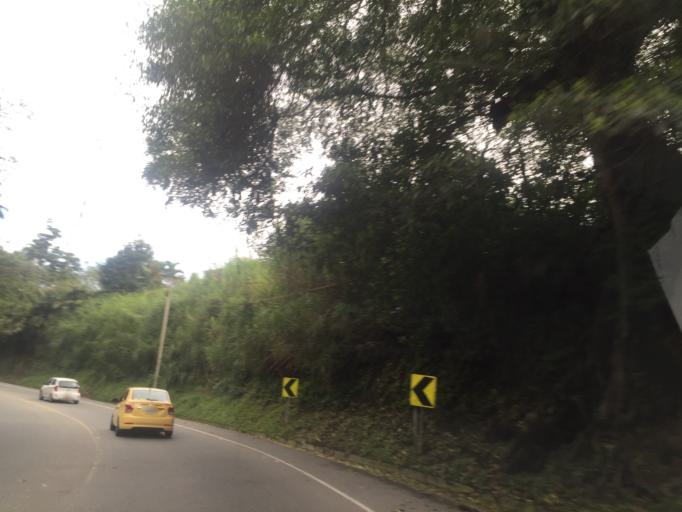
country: CO
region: Quindio
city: Montenegro
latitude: 4.5379
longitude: -75.7426
